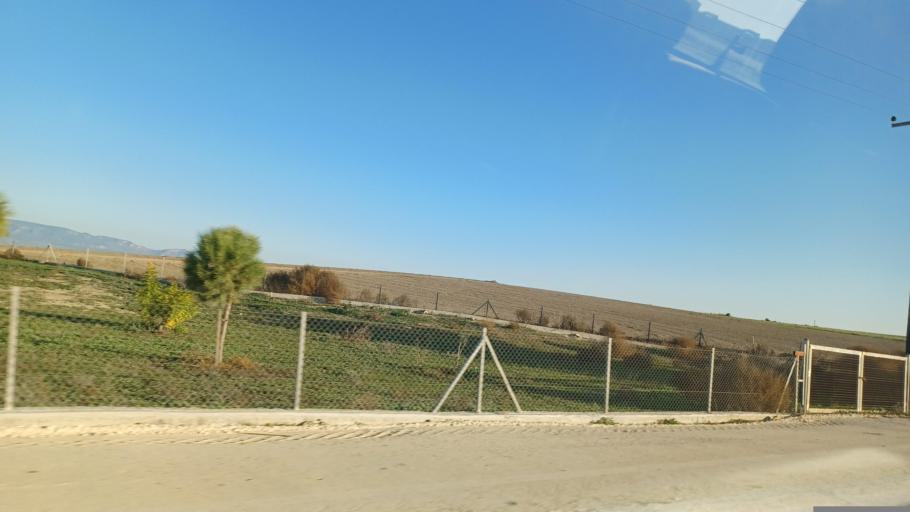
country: CY
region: Lefkosia
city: Mammari
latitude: 35.1547
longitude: 33.2504
